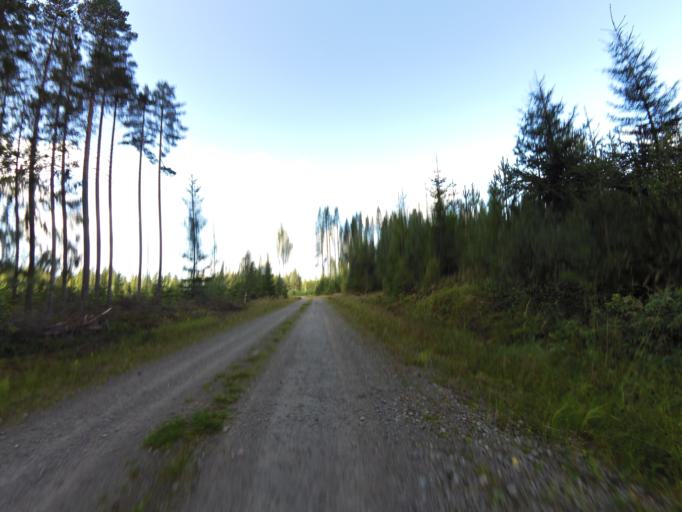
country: SE
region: Gaevleborg
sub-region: Ockelbo Kommun
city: Ockelbo
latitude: 60.8126
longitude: 16.7653
